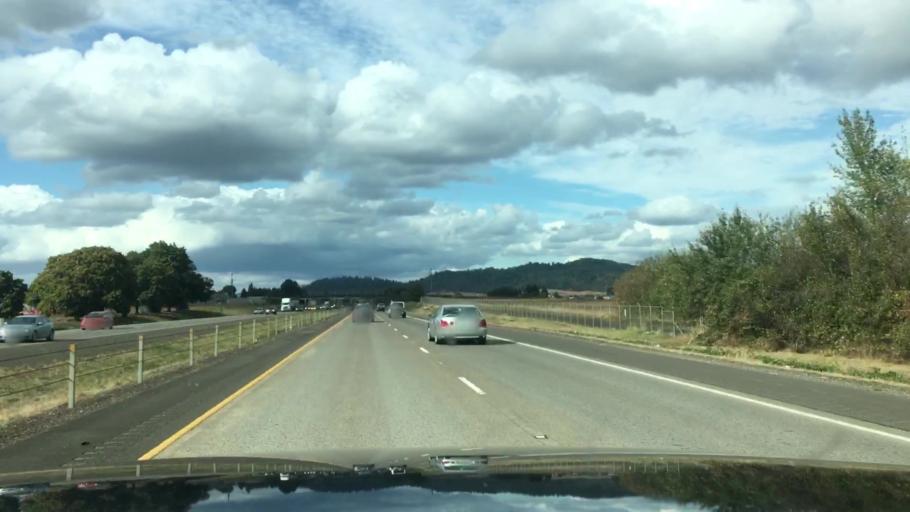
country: US
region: Oregon
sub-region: Lane County
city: Creswell
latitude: 43.9344
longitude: -123.0092
